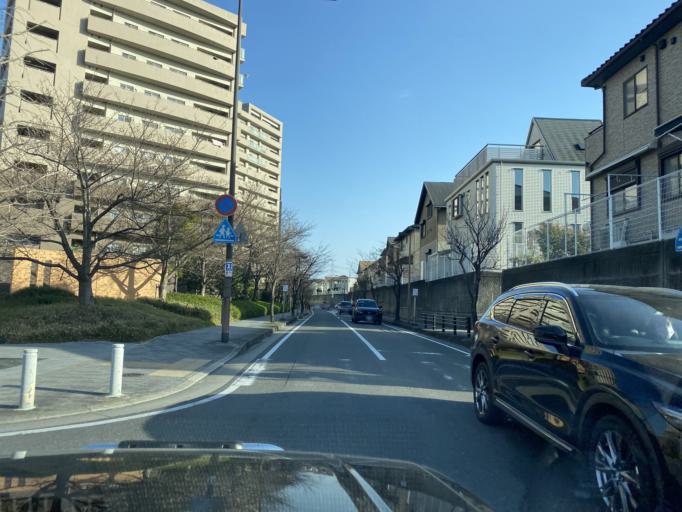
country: JP
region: Kyoto
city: Yawata
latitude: 34.8383
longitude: 135.7190
